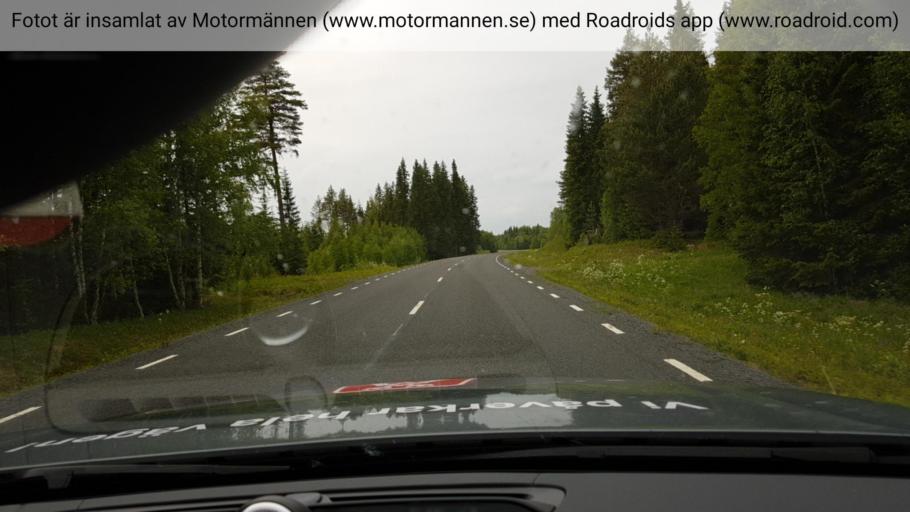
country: SE
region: Jaemtland
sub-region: Stroemsunds Kommun
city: Stroemsund
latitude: 63.6359
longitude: 15.1946
